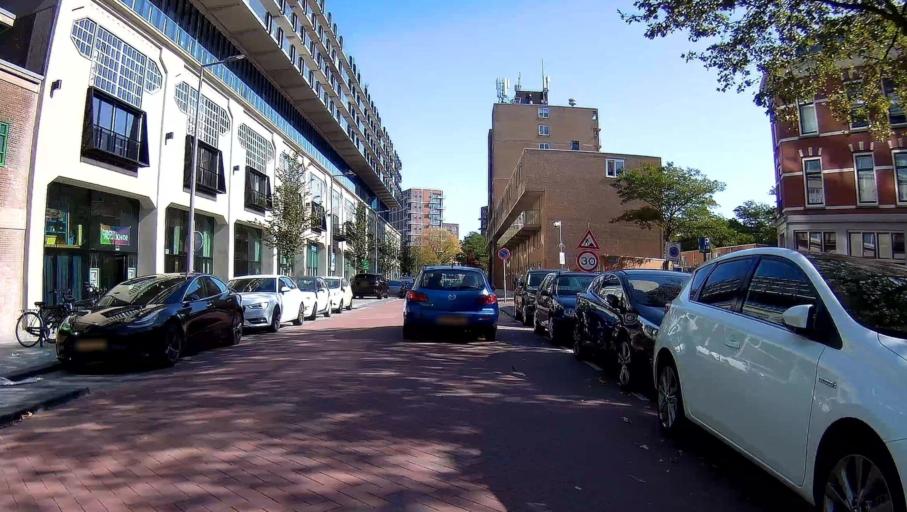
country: NL
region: South Holland
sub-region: Gemeente Rotterdam
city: Rotterdam
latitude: 51.9016
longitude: 4.4865
